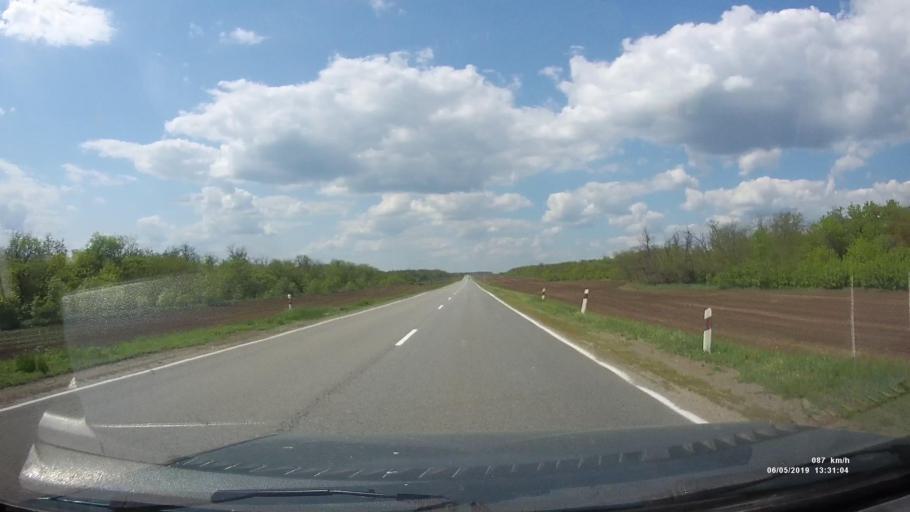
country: RU
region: Rostov
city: Ust'-Donetskiy
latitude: 47.6738
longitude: 40.8166
